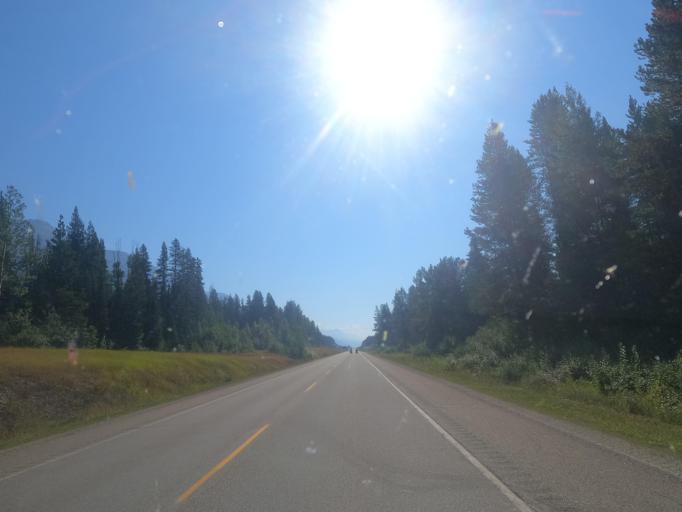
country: CA
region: Alberta
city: Grande Cache
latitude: 52.9888
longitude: -119.0046
